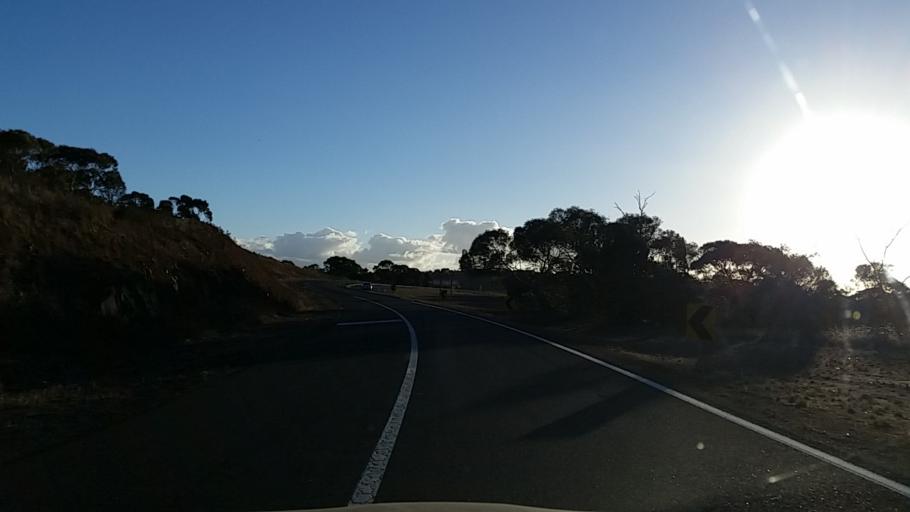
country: AU
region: South Australia
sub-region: Mount Barker
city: Callington
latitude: -35.1285
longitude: 139.0400
